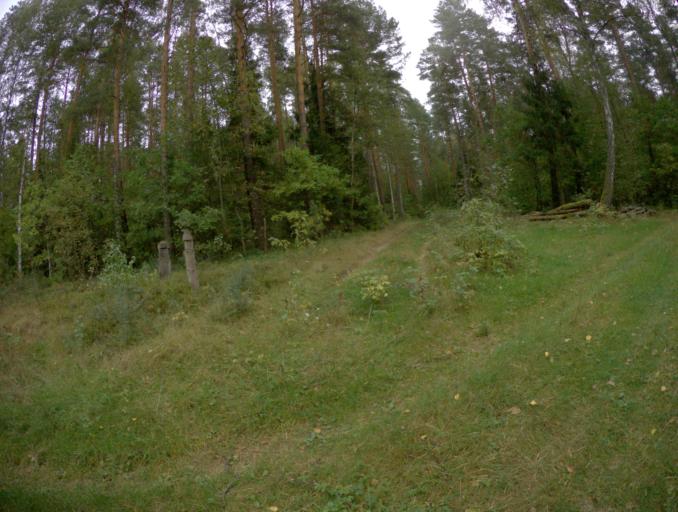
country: RU
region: Vladimir
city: Bogolyubovo
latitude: 56.1423
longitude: 40.5589
